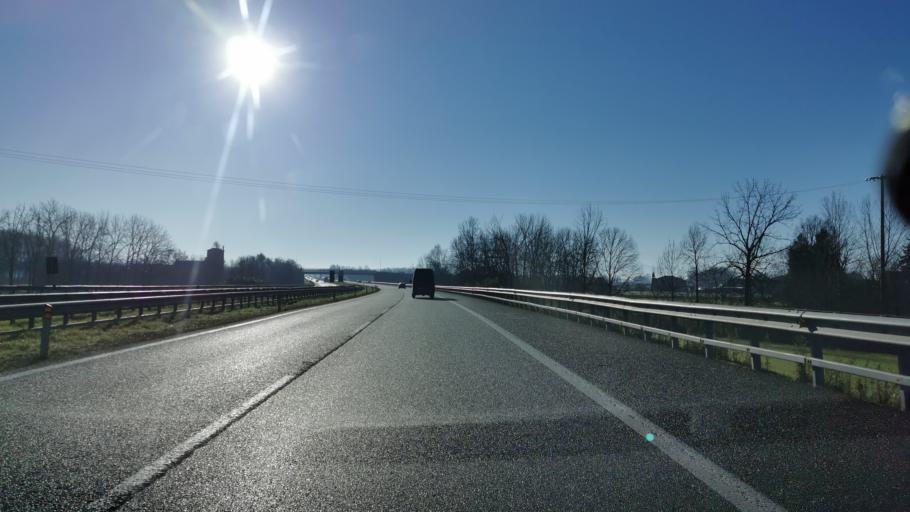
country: IT
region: Piedmont
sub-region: Provincia di Torino
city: Villastellone
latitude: 44.9486
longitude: 7.7134
